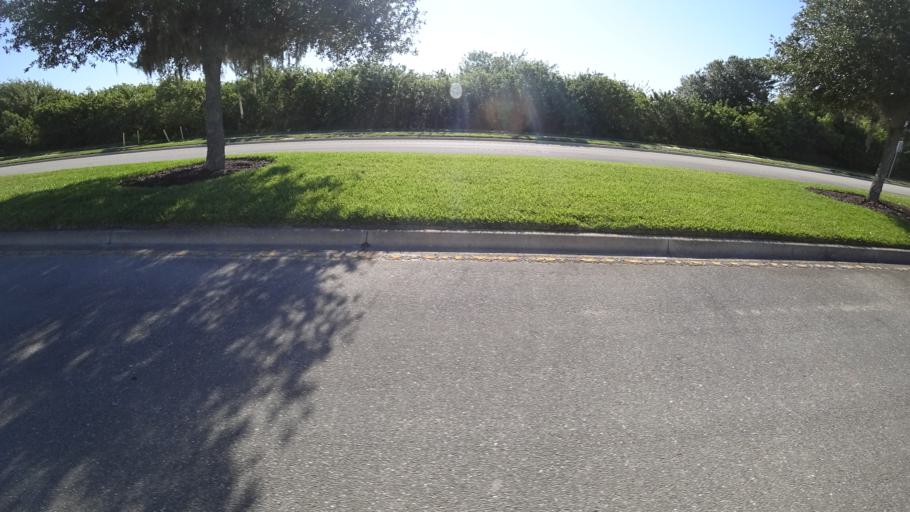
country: US
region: Florida
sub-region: Sarasota County
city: The Meadows
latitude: 27.3881
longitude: -82.3530
